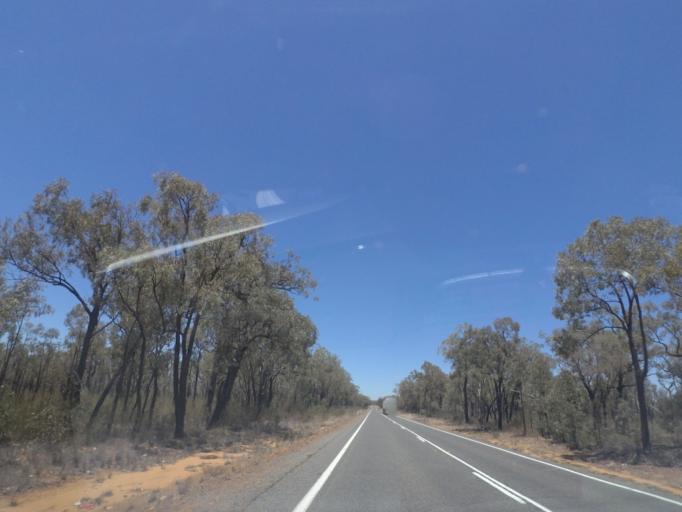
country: AU
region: New South Wales
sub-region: Narrabri
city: Narrabri
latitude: -30.7051
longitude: 149.5325
